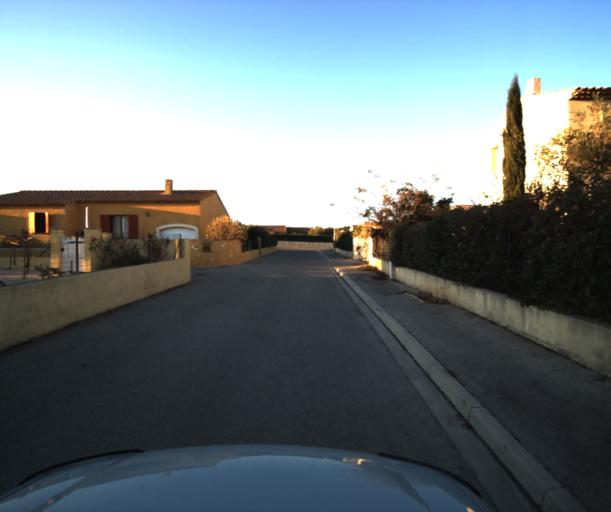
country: FR
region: Provence-Alpes-Cote d'Azur
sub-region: Departement du Vaucluse
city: Pertuis
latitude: 43.6990
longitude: 5.4968
